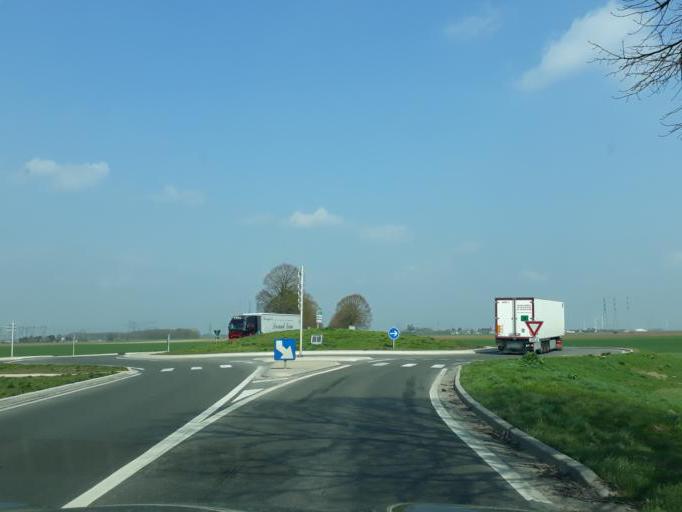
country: FR
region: Centre
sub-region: Departement du Loiret
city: Artenay
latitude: 48.0951
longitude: 1.8652
